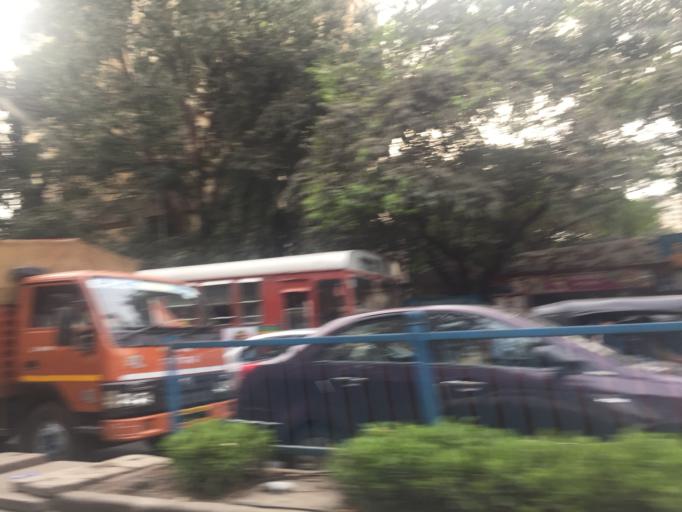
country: IN
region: Maharashtra
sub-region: Mumbai Suburban
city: Powai
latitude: 19.1247
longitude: 72.9253
